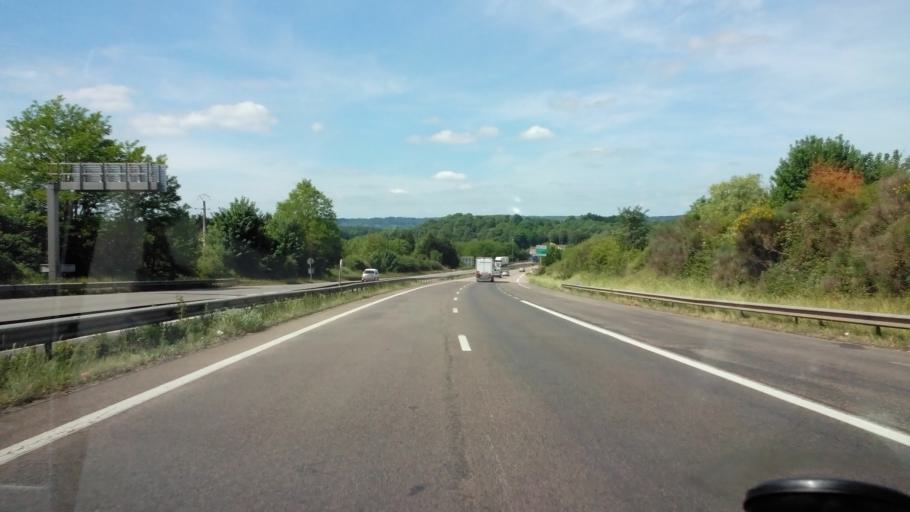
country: FR
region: Lorraine
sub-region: Departement de Meurthe-et-Moselle
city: Dommartin-les-Toul
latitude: 48.6581
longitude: 5.9060
